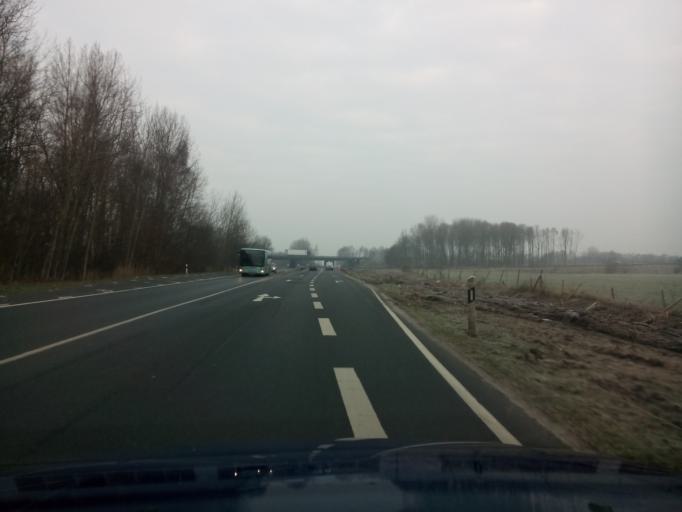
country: DE
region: Lower Saxony
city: Loxstedt
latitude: 53.4618
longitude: 8.6026
